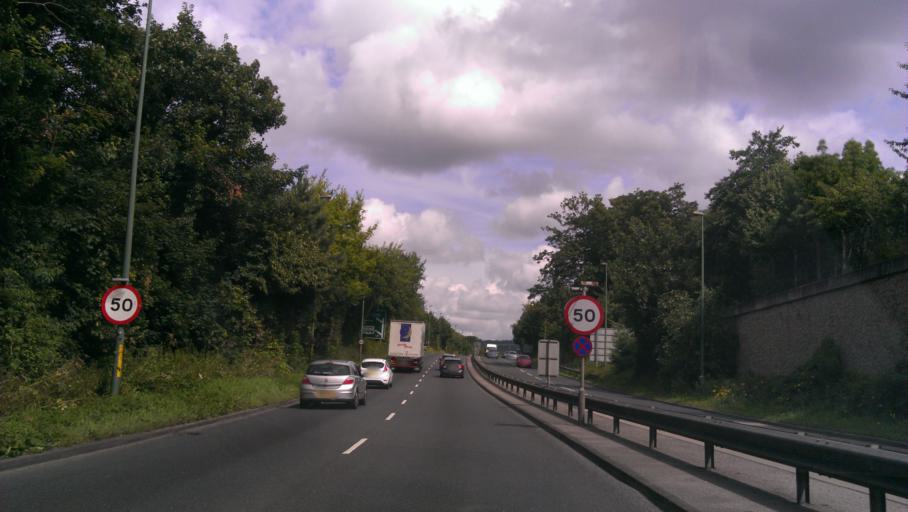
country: GB
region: England
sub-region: Kent
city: Maidstone
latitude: 51.2854
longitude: 0.5182
